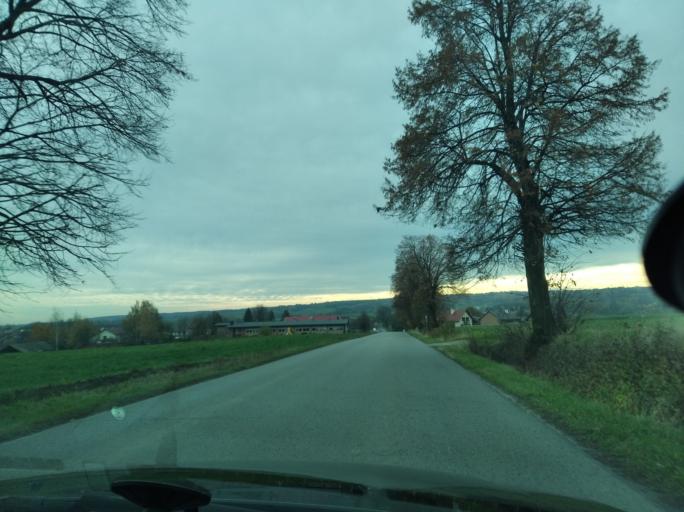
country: PL
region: Subcarpathian Voivodeship
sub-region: Powiat lancucki
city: Wysoka
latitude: 50.0216
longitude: 22.2601
